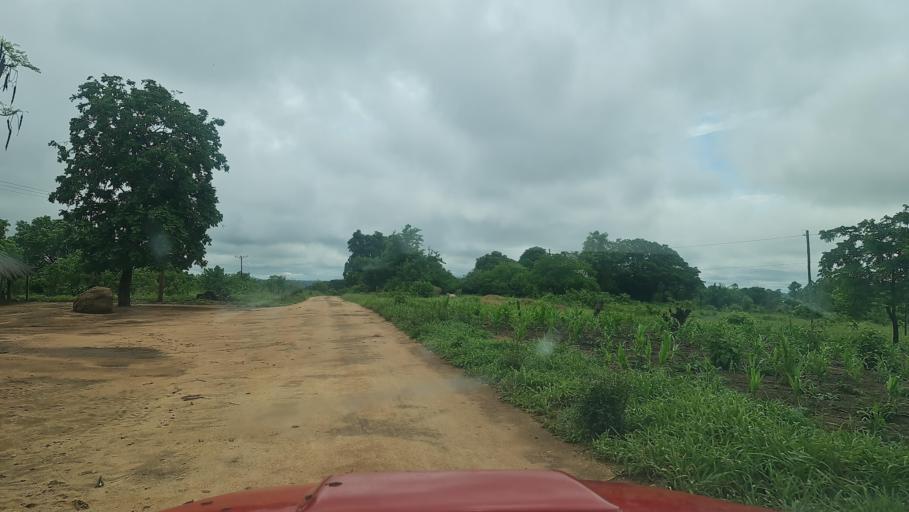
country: MW
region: Southern Region
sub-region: Nsanje District
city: Nsanje
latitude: -17.1809
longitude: 35.9081
